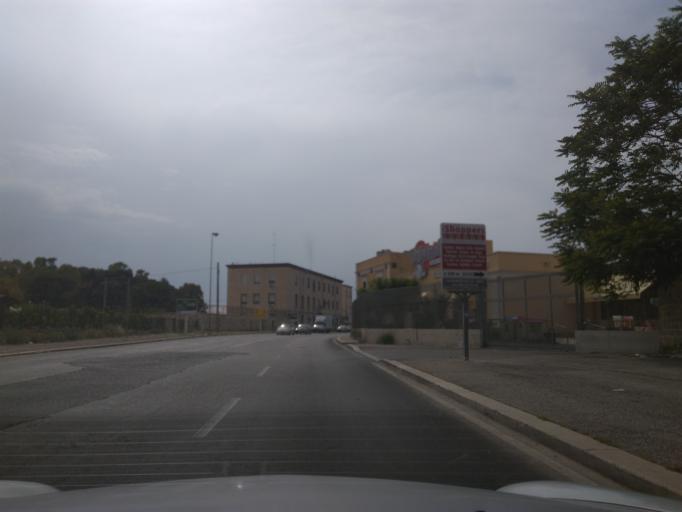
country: IT
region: Apulia
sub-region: Provincia di Bari
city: Bari
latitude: 41.1277
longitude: 16.8403
